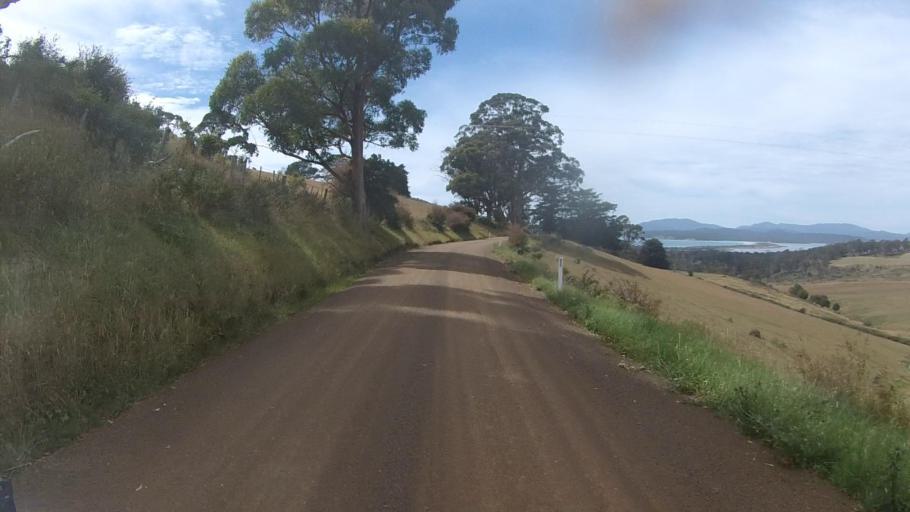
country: AU
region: Tasmania
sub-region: Sorell
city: Sorell
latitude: -42.7948
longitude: 147.8393
